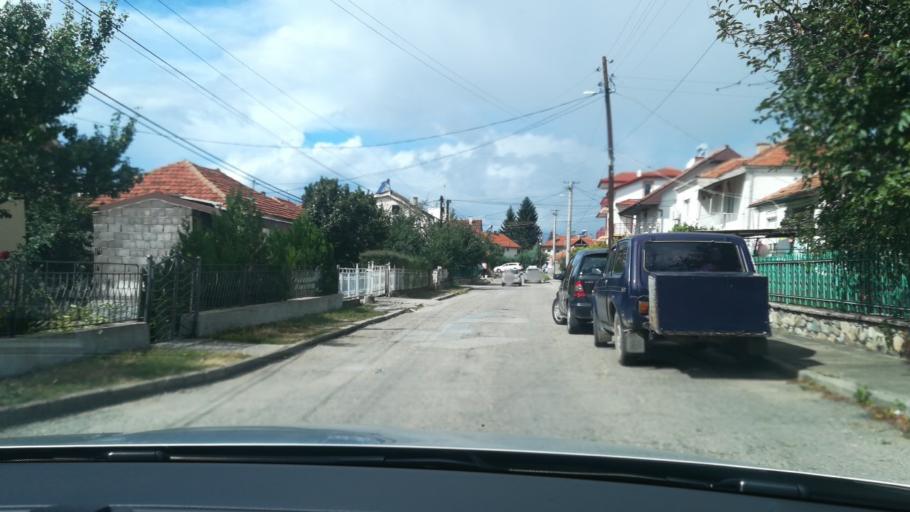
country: MK
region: Delcevo
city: Delcevo
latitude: 41.9647
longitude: 22.7769
